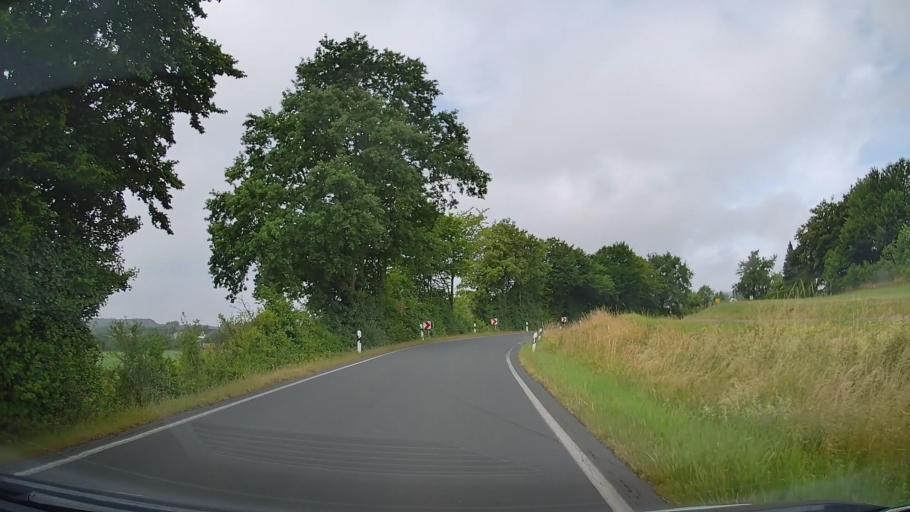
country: DE
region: North Rhine-Westphalia
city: Porta Westfalica
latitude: 52.2227
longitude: 8.9616
